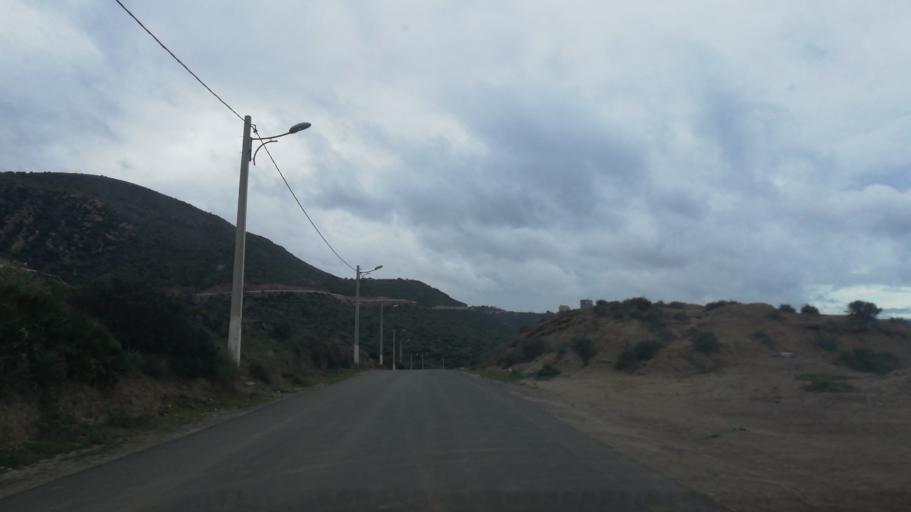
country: DZ
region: Oran
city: Bir el Djir
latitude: 35.7736
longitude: -0.5168
